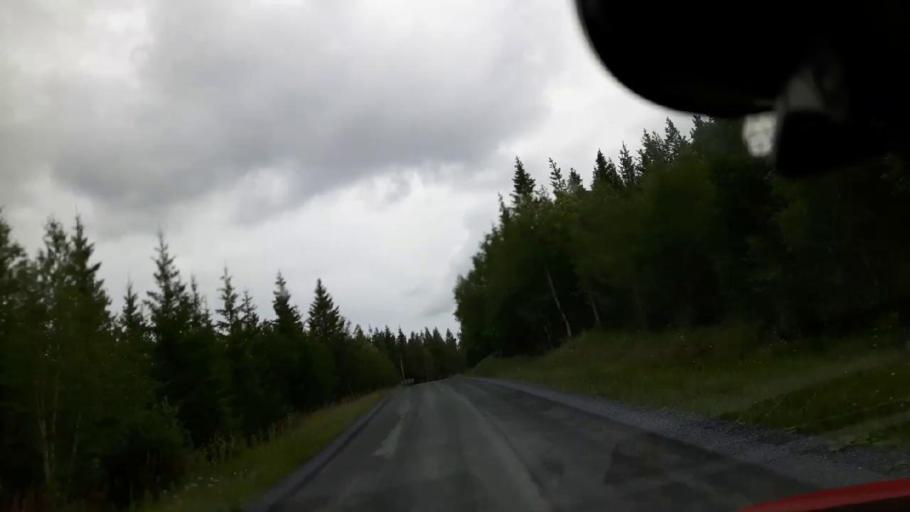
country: SE
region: Jaemtland
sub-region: Krokoms Kommun
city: Valla
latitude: 63.3830
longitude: 13.8843
